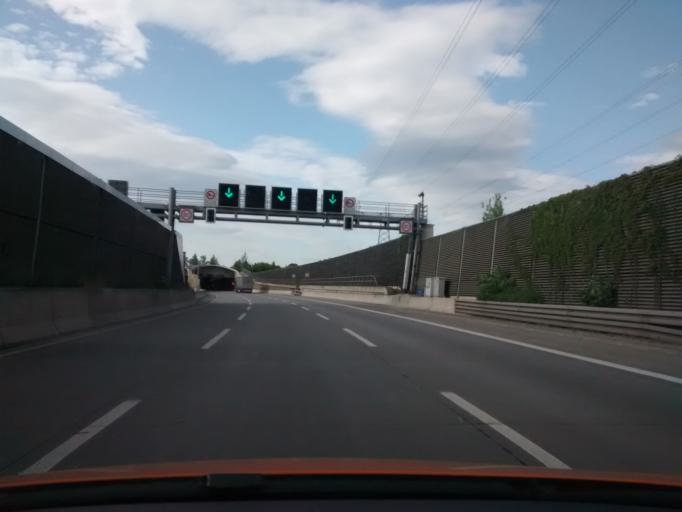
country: DE
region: Berlin
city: Altglienicke
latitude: 52.4016
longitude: 13.5206
